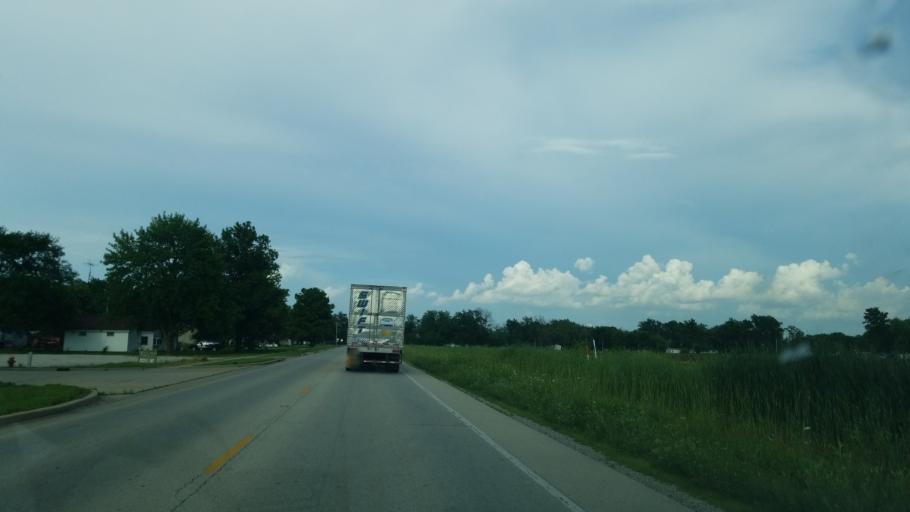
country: US
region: Illinois
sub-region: Marion County
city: Sandoval
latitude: 38.6163
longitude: -89.1309
